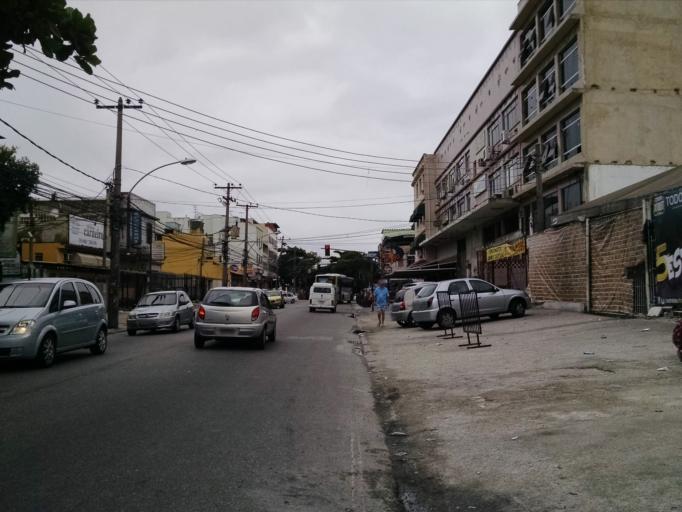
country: BR
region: Rio de Janeiro
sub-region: Duque De Caxias
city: Duque de Caxias
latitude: -22.8342
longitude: -43.3187
